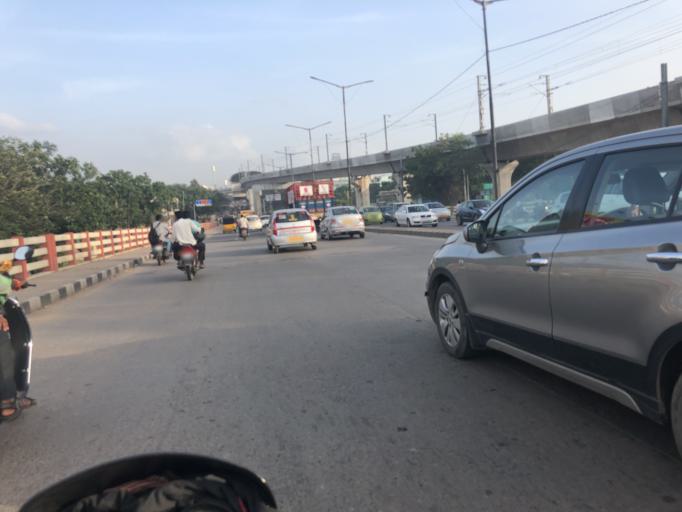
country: IN
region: Telangana
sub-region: Rangareddi
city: Kukatpalli
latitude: 17.4606
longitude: 78.4320
